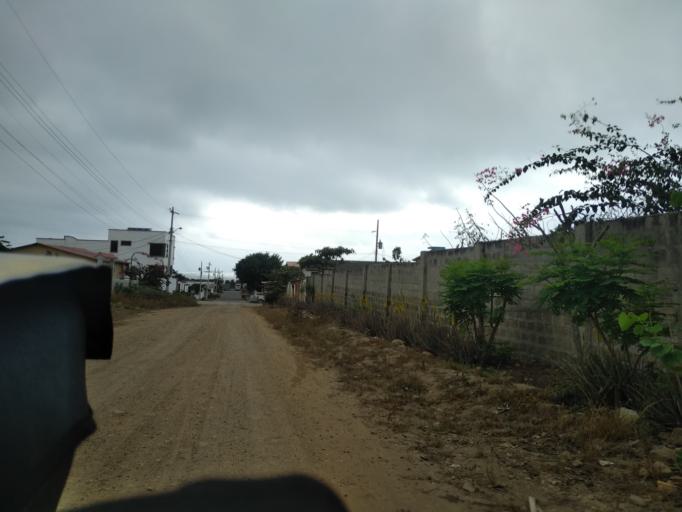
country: EC
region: Santa Elena
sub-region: Canton Santa Elena
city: Santa Elena
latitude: -2.2038
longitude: -80.8691
